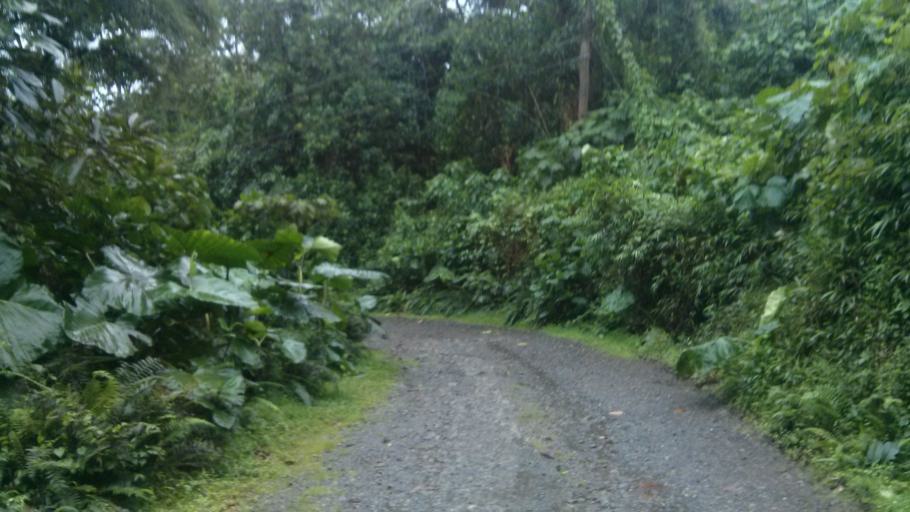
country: CR
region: San Jose
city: Ipis
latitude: 10.0314
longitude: -83.9421
